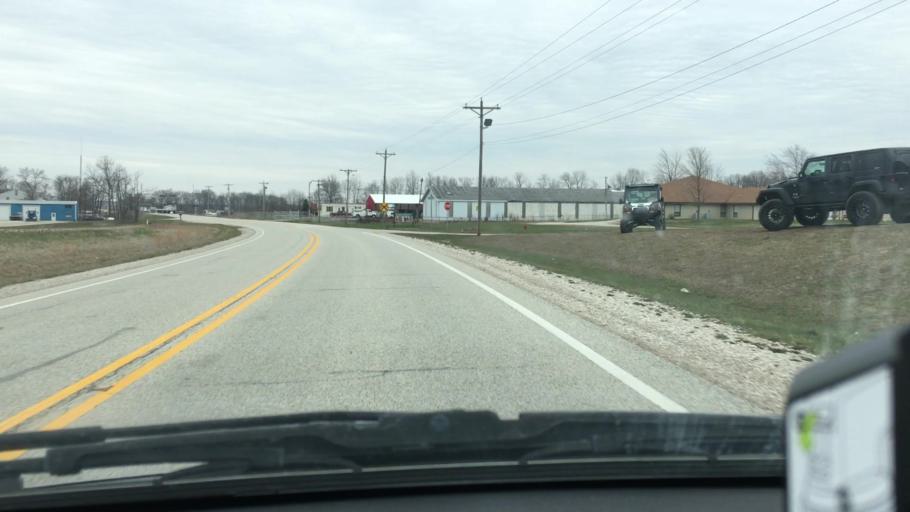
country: US
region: Indiana
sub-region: Greene County
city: Bloomfield
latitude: 39.0259
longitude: -87.0118
